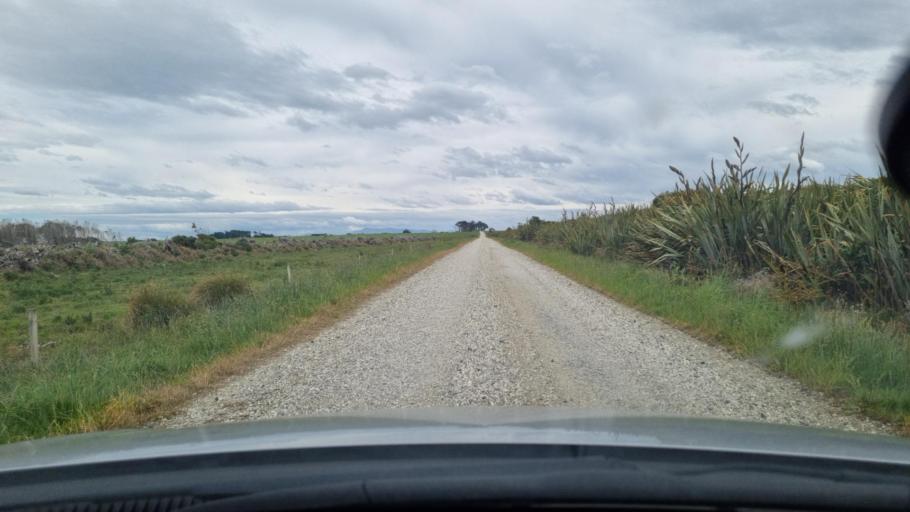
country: NZ
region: Southland
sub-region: Invercargill City
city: Invercargill
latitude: -46.3937
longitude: 168.2711
